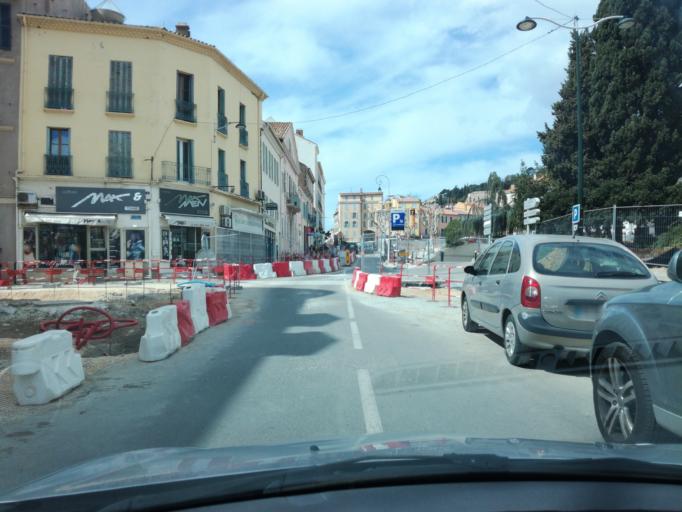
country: FR
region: Provence-Alpes-Cote d'Azur
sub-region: Departement du Var
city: Hyeres
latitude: 43.1208
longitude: 6.1329
